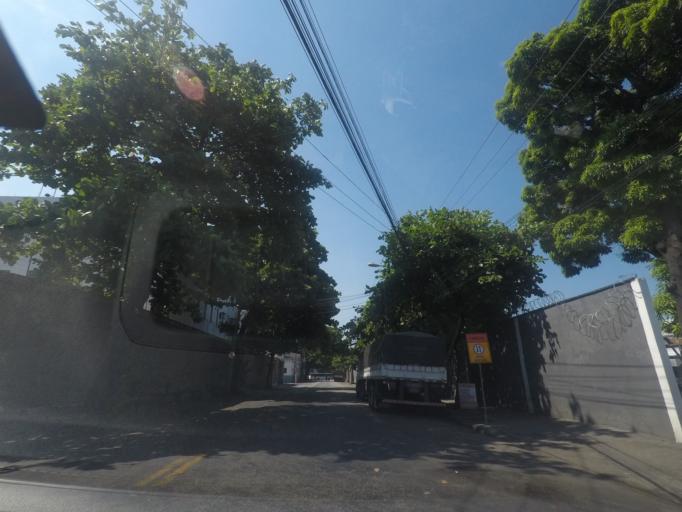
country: BR
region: Rio de Janeiro
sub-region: Rio De Janeiro
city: Rio de Janeiro
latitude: -22.8922
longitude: -43.2189
